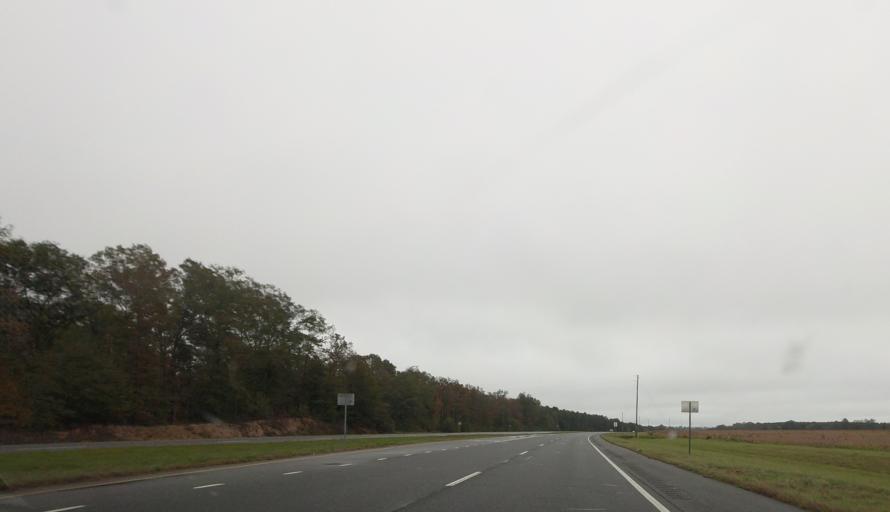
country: US
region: Georgia
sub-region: Taylor County
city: Reynolds
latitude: 32.5575
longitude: -84.0667
